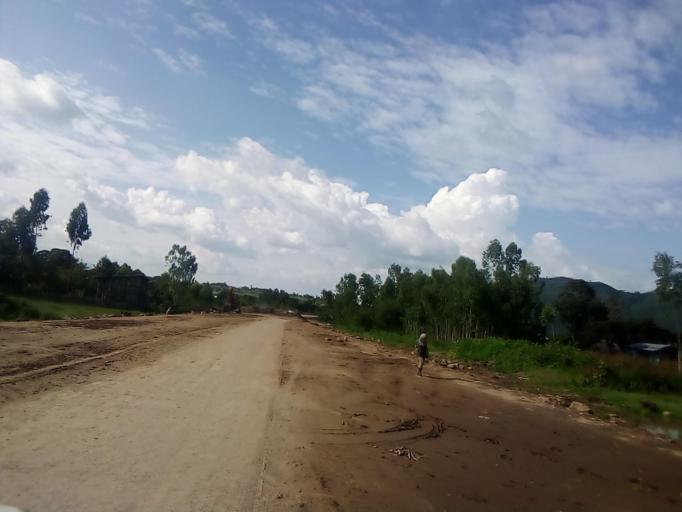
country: ET
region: Southern Nations, Nationalities, and People's Region
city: K'olito
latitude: 7.6177
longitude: 38.0639
